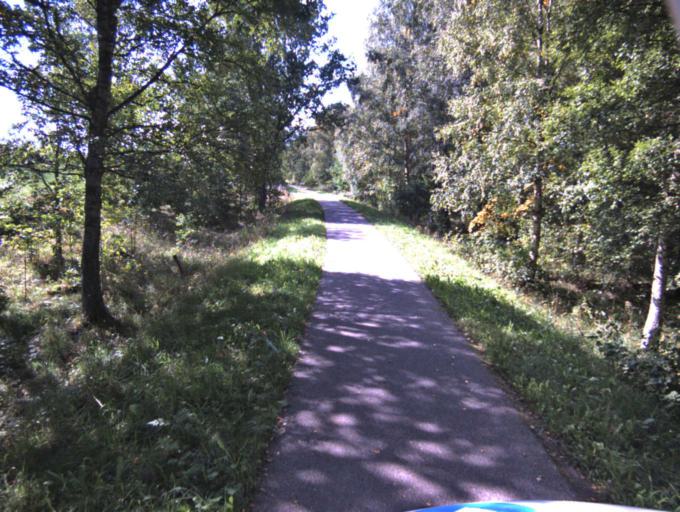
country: SE
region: Vaestra Goetaland
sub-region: Ulricehamns Kommun
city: Ulricehamn
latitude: 57.8388
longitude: 13.3199
